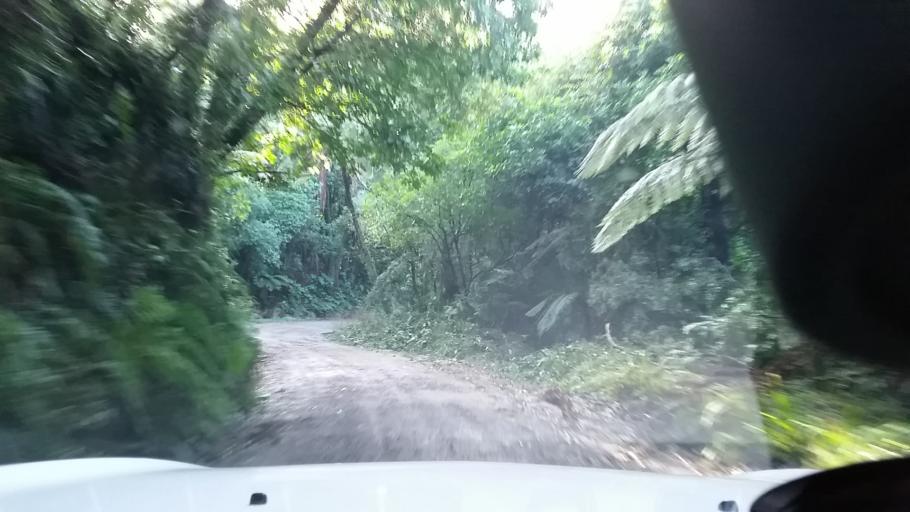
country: NZ
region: Bay of Plenty
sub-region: Kawerau District
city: Kawerau
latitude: -38.0192
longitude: 176.5799
